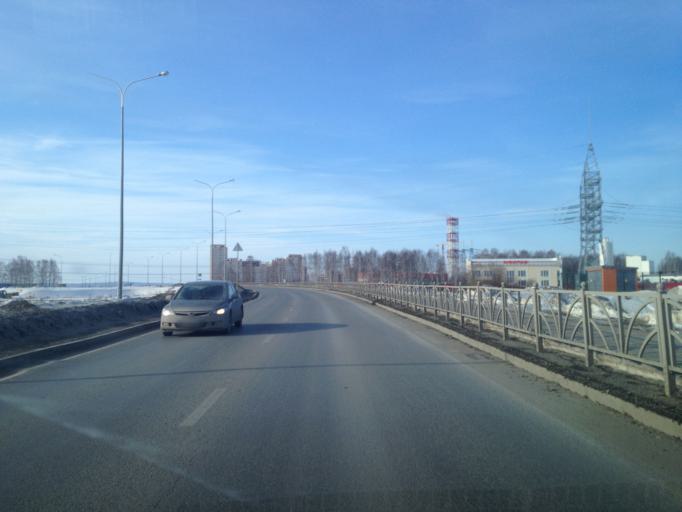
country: RU
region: Sverdlovsk
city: Sovkhoznyy
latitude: 56.7516
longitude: 60.5796
